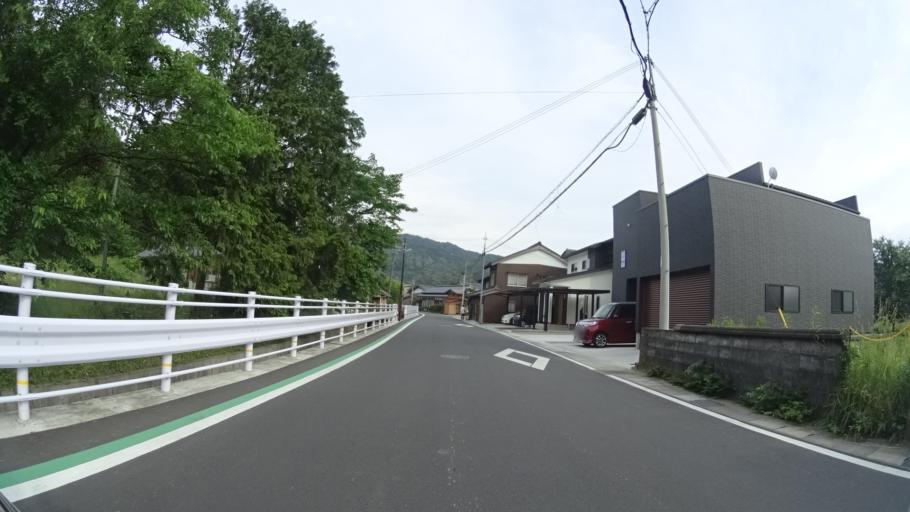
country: JP
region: Kyoto
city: Miyazu
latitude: 35.5311
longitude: 135.1249
